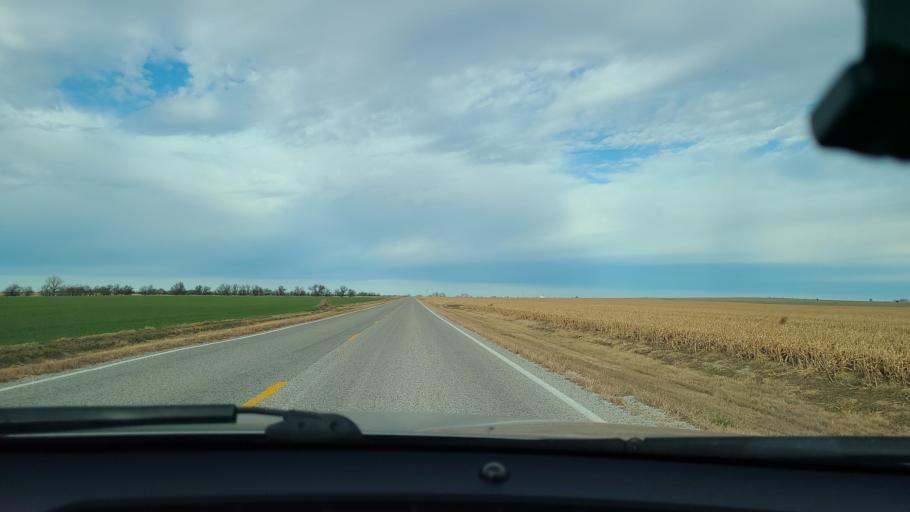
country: US
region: Kansas
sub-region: McPherson County
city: Inman
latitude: 38.3211
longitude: -97.9246
